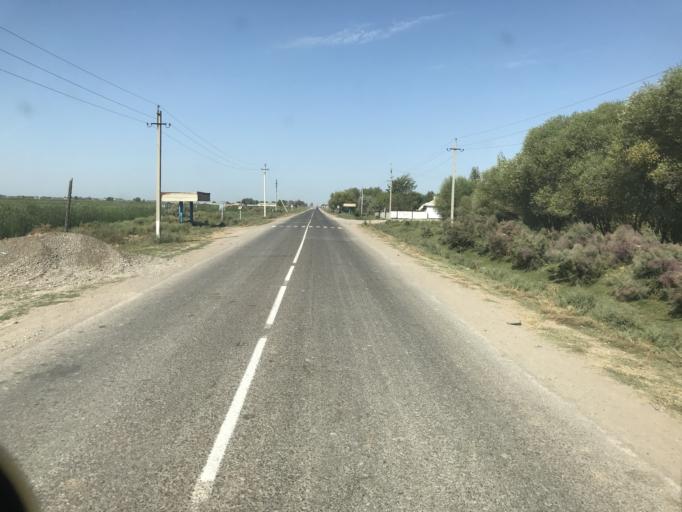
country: KZ
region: Ongtustik Qazaqstan
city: Myrzakent
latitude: 40.6854
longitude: 68.5705
